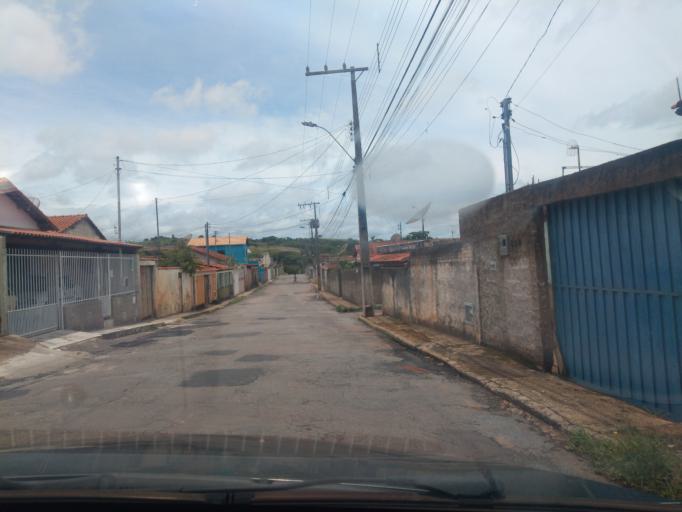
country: BR
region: Minas Gerais
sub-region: Tres Coracoes
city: Tres Coracoes
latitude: -21.6820
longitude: -45.2598
